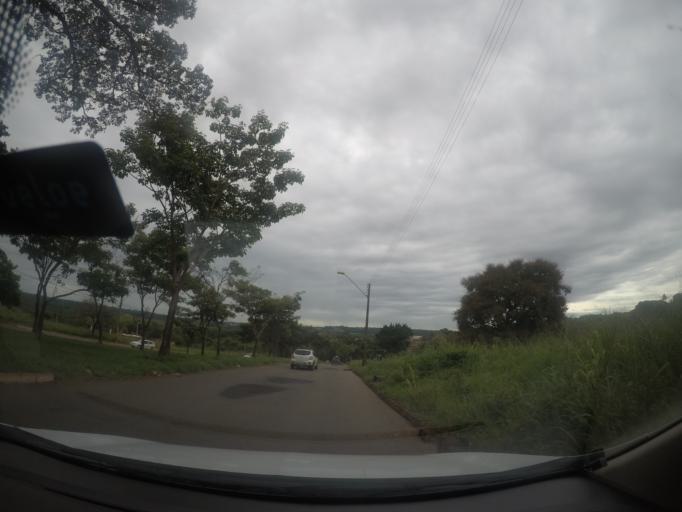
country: BR
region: Goias
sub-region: Goiania
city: Goiania
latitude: -16.6055
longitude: -49.3000
